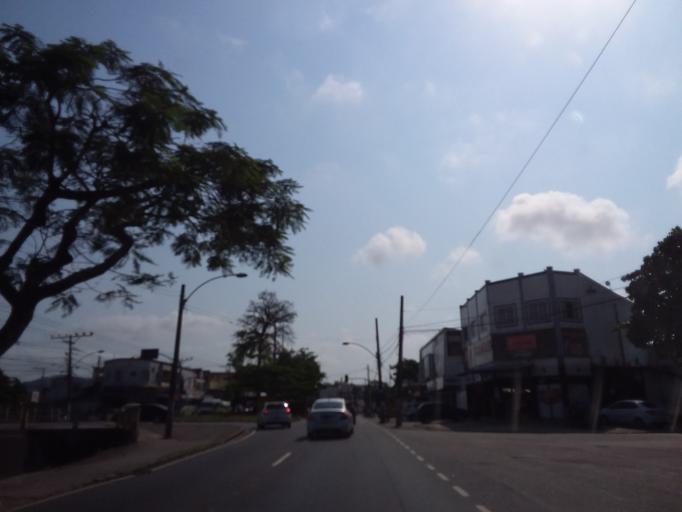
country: BR
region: Rio de Janeiro
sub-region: Nilopolis
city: Nilopolis
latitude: -22.9022
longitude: -43.5487
